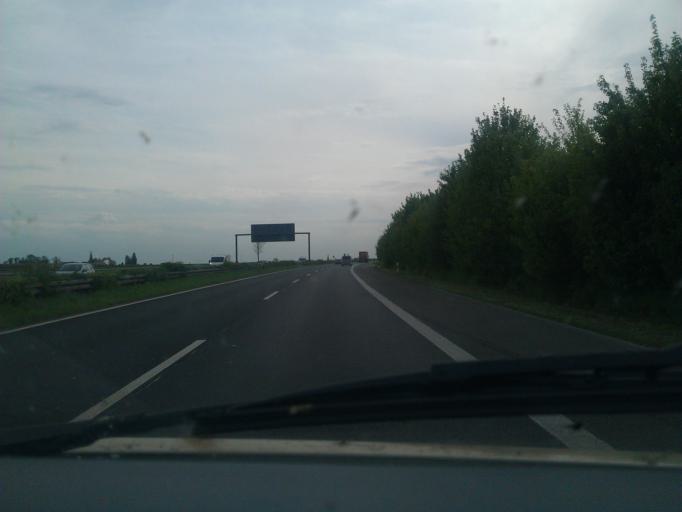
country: DE
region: North Rhine-Westphalia
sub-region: Regierungsbezirk Koln
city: Titz
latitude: 51.0282
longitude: 6.4540
